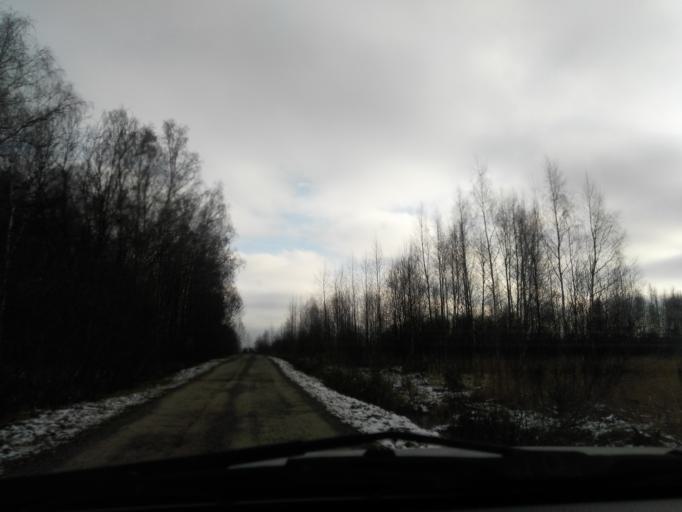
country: RU
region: Moskovskaya
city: Troitsk
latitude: 55.3693
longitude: 37.1682
